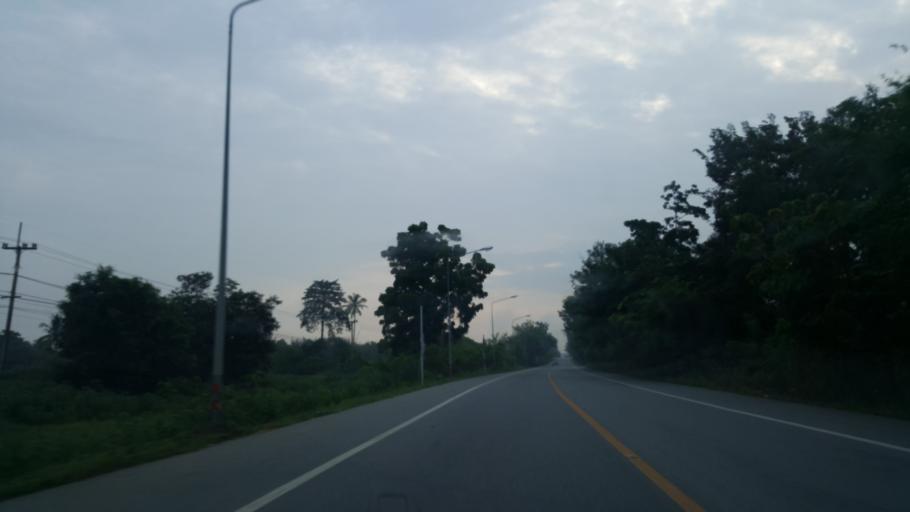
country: TH
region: Chon Buri
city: Sattahip
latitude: 12.7329
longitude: 100.9207
